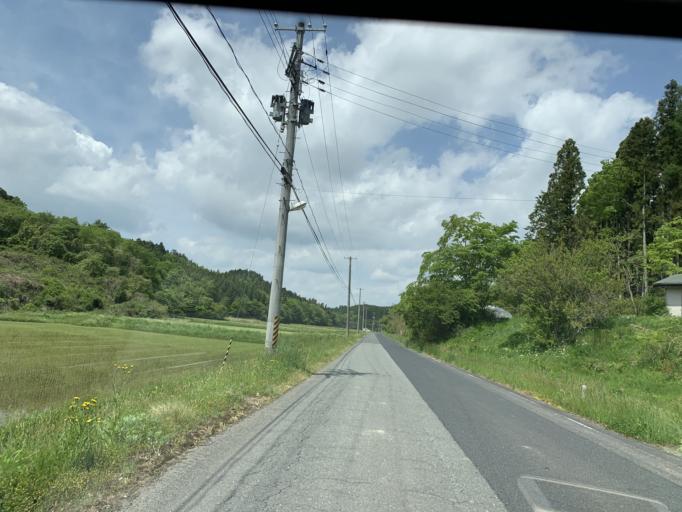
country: JP
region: Miyagi
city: Furukawa
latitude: 38.7726
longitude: 140.9693
